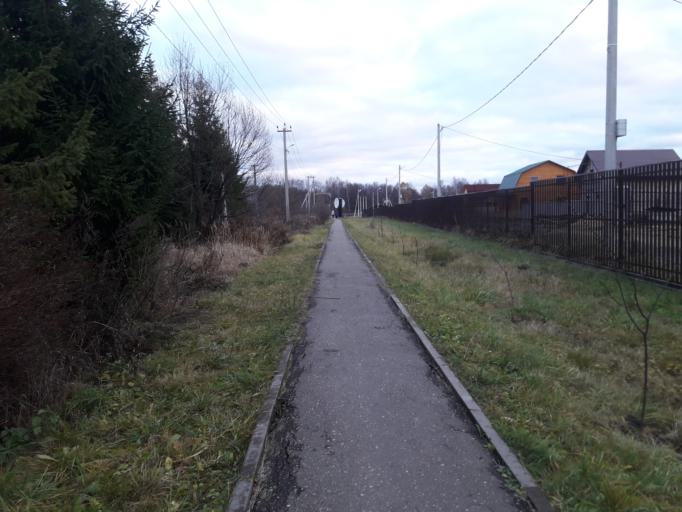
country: RU
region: Moskovskaya
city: Ashukino
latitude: 56.1724
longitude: 37.9376
